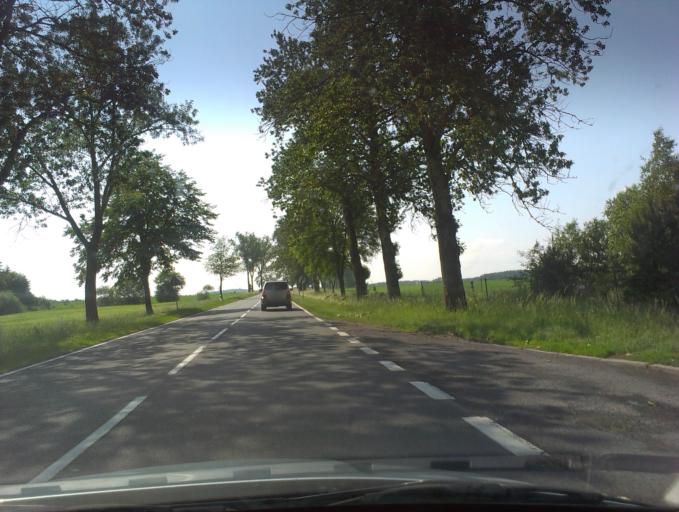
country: PL
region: Greater Poland Voivodeship
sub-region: Powiat zlotowski
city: Okonek
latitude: 53.5655
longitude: 16.8321
